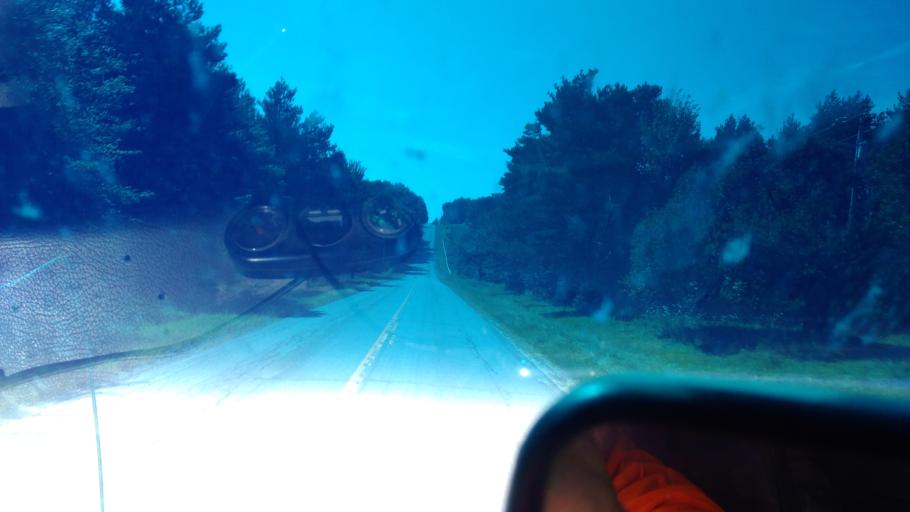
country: US
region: New York
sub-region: Allegany County
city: Andover
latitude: 42.1194
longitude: -77.7915
